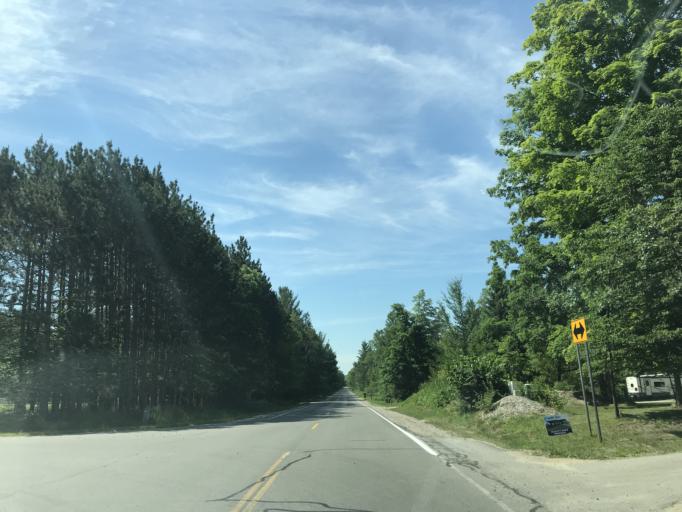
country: US
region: Michigan
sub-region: Grand Traverse County
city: Traverse City
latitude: 44.6546
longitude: -85.7169
